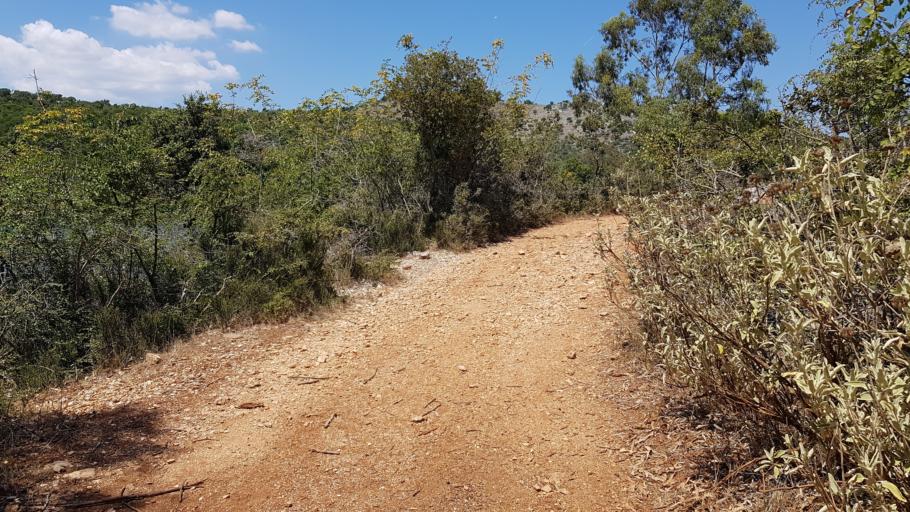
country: AL
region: Vlore
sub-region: Rrethi i Sarandes
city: Xarre
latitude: 39.7535
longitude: 19.9979
